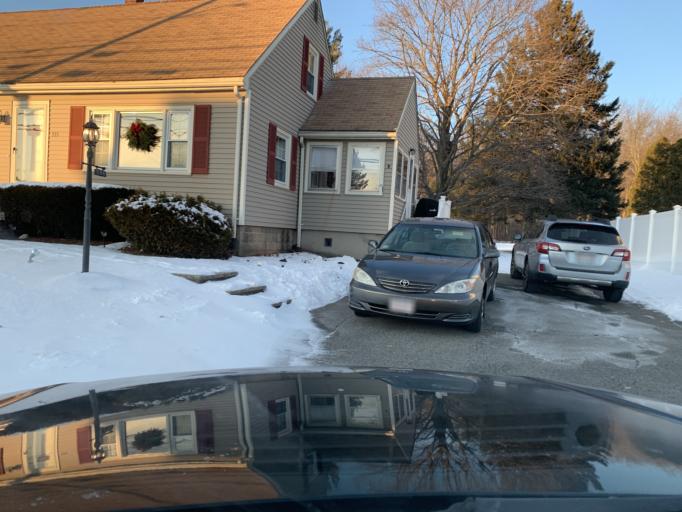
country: US
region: Massachusetts
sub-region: Essex County
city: Haverhill
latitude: 42.7819
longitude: -71.1099
